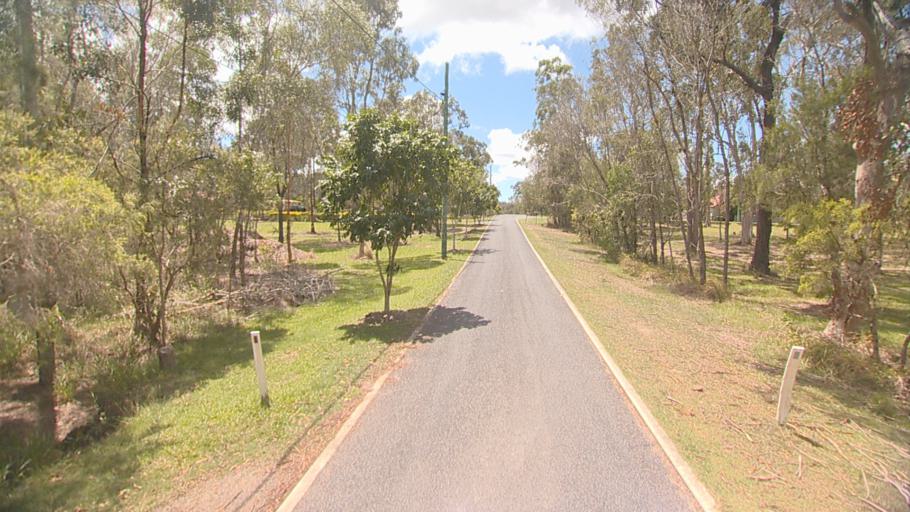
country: AU
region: Queensland
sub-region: Logan
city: Beenleigh
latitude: -27.6603
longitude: 153.2299
